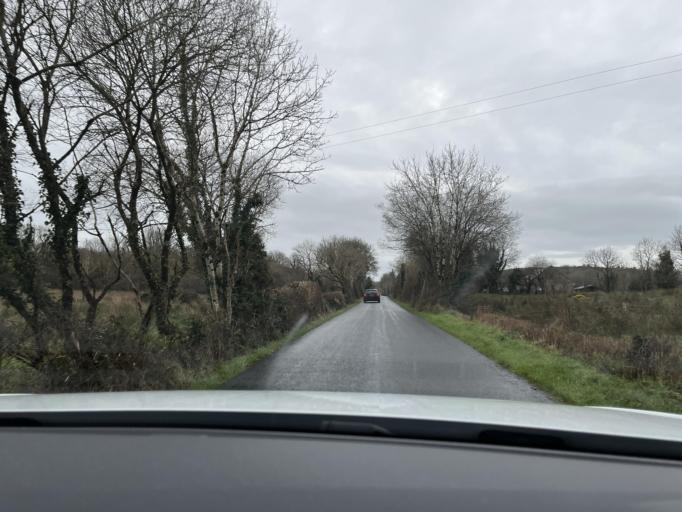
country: IE
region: Connaught
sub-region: County Leitrim
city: Manorhamilton
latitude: 54.2571
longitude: -8.2404
